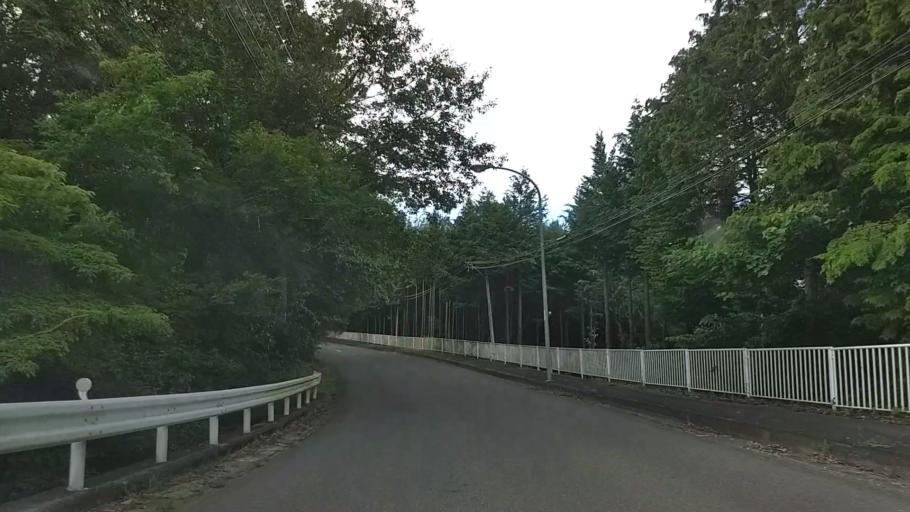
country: JP
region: Yamanashi
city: Uenohara
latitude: 35.5887
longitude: 139.1504
